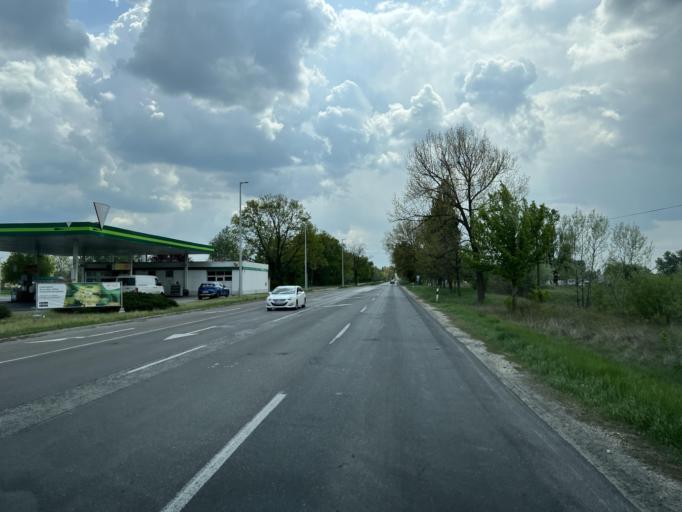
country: HU
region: Pest
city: Cegled
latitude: 47.1475
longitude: 19.7893
